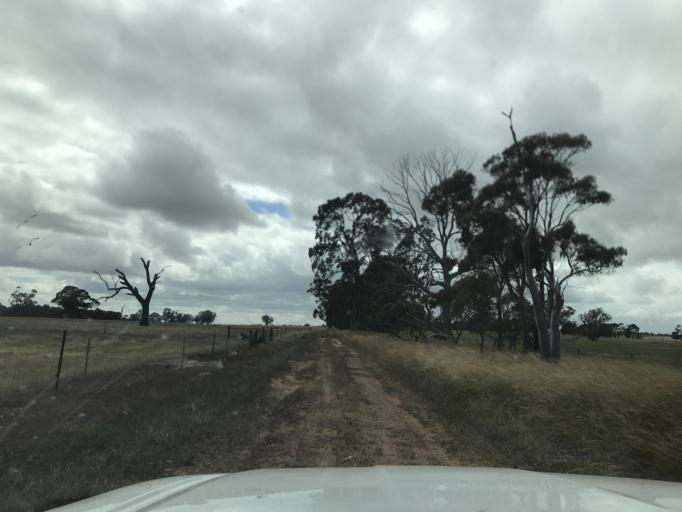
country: AU
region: South Australia
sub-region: Naracoorte and Lucindale
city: Naracoorte
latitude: -36.9008
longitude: 141.4053
